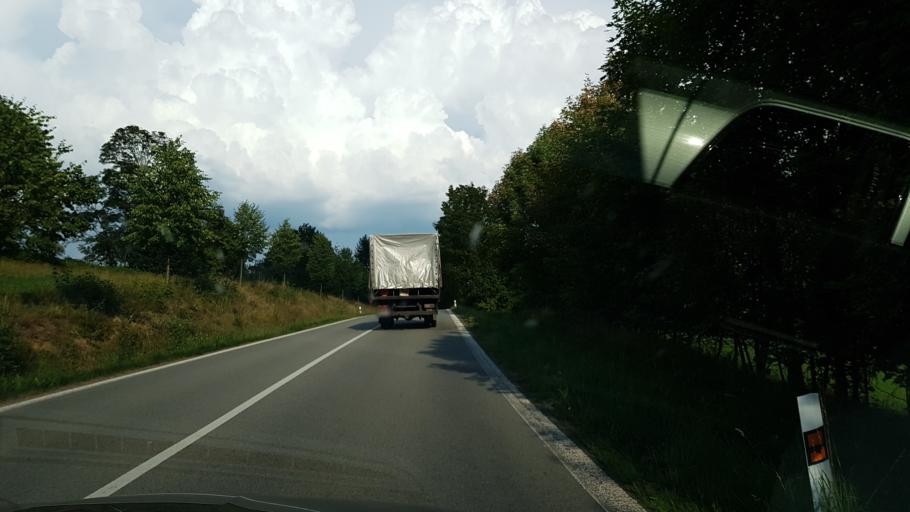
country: CZ
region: Pardubicky
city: Jablonne nad Orlici
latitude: 50.0922
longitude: 16.6068
